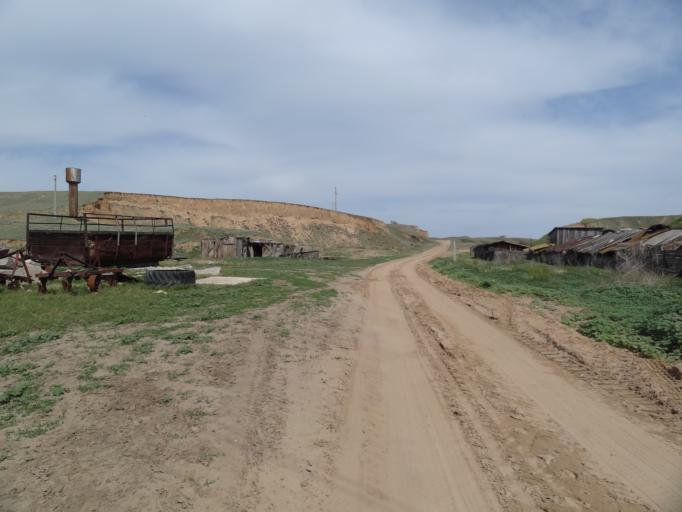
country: RU
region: Saratov
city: Privolzhskiy
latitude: 51.2044
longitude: 45.9204
